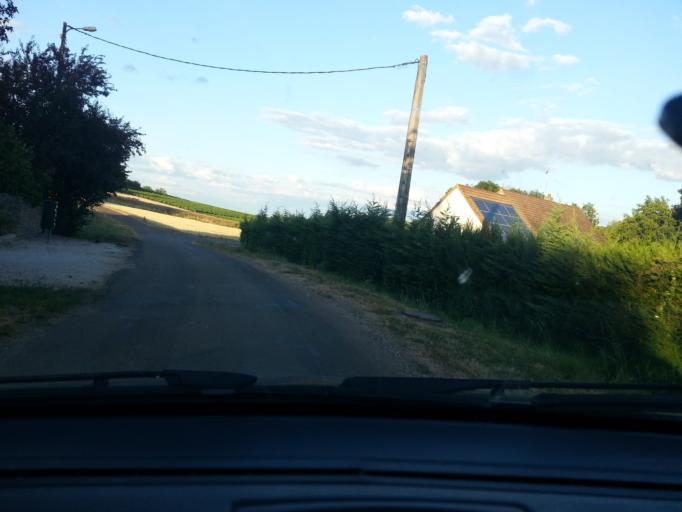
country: FR
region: Bourgogne
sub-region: Departement de Saone-et-Loire
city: Buxy
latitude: 46.7531
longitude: 4.6844
